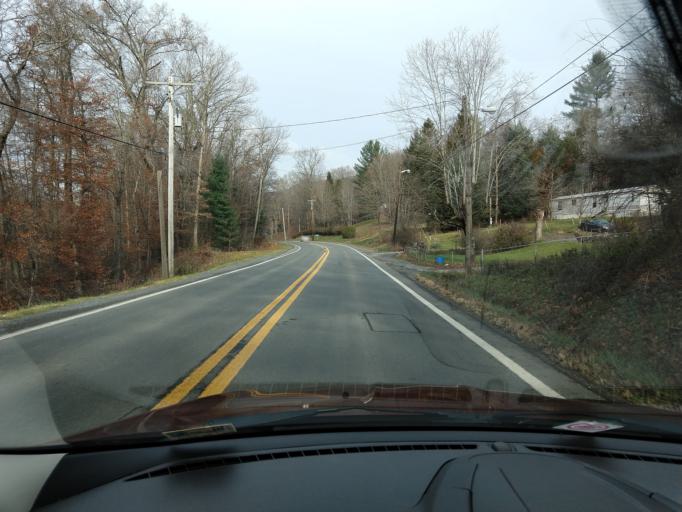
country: US
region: West Virginia
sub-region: Greenbrier County
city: Rainelle
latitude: 37.9778
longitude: -80.7113
